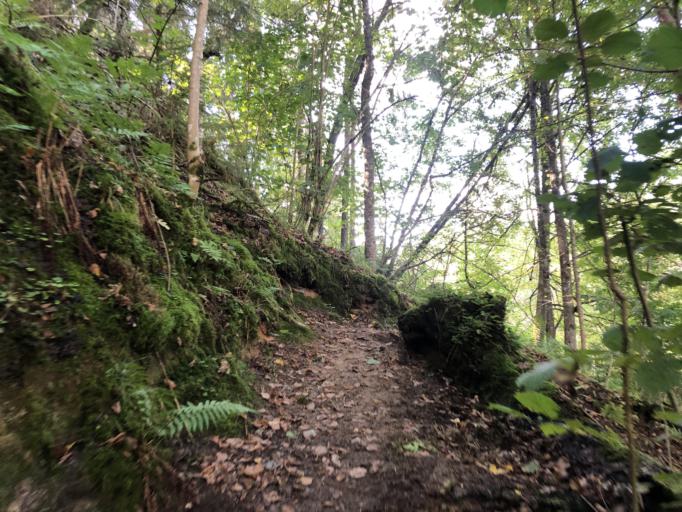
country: LV
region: Priekuli
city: Priekuli
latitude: 57.3562
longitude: 25.3286
